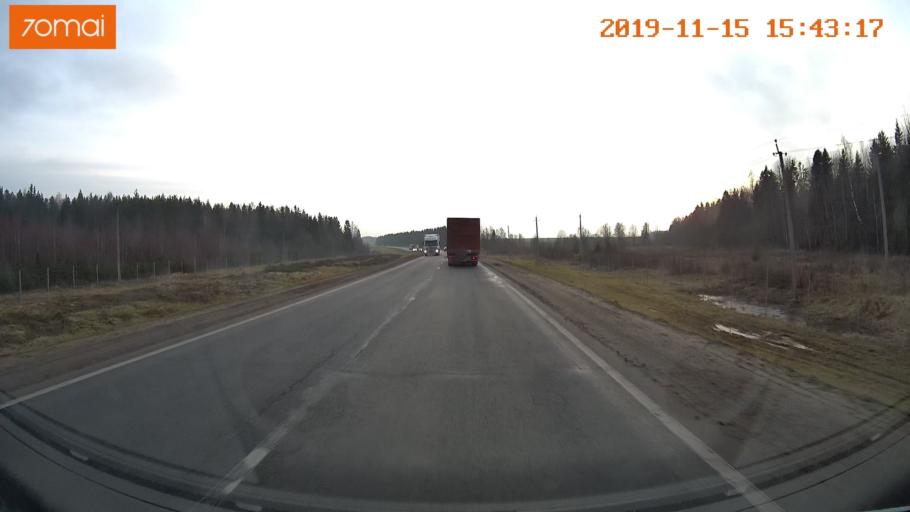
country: RU
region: Jaroslavl
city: Danilov
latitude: 57.9841
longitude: 40.0295
